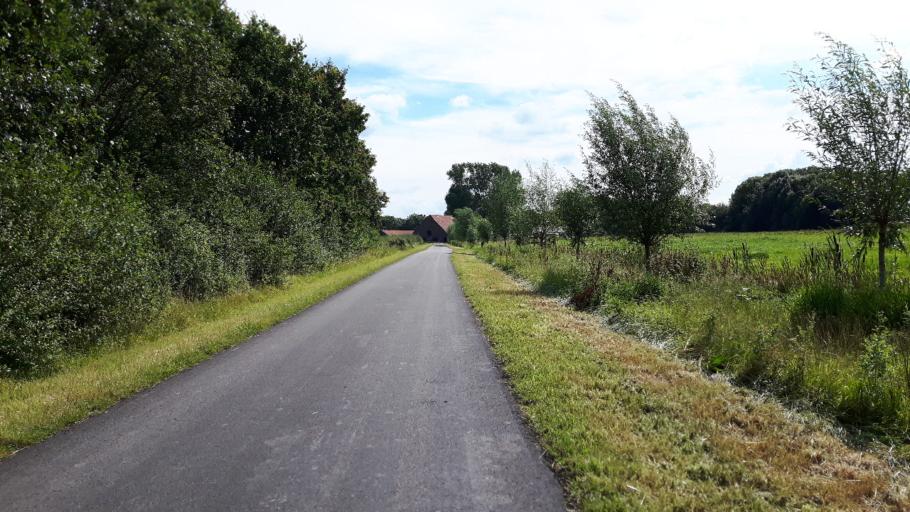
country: NL
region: Utrecht
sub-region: Stichtse Vecht
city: Spechtenkamp
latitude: 52.1262
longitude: 5.0009
